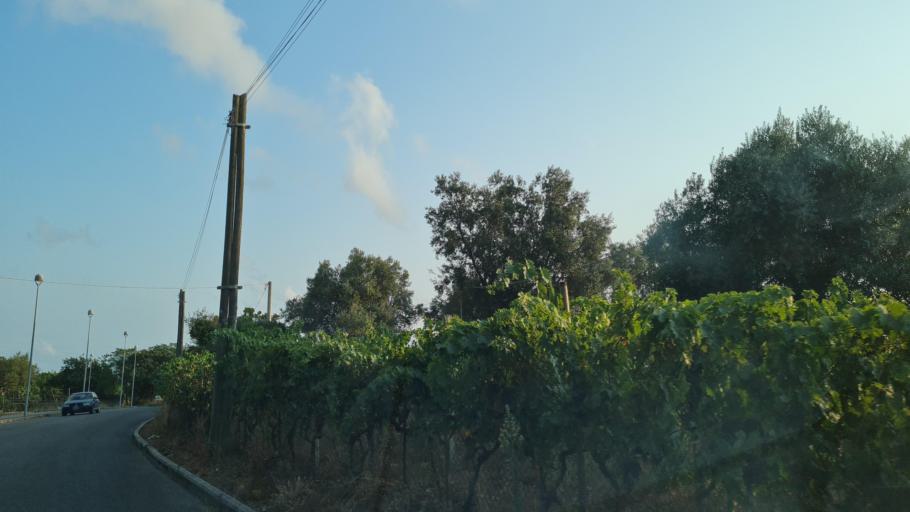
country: IT
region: Latium
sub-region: Provincia di Viterbo
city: Montalto di Castro
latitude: 42.3370
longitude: 11.6123
